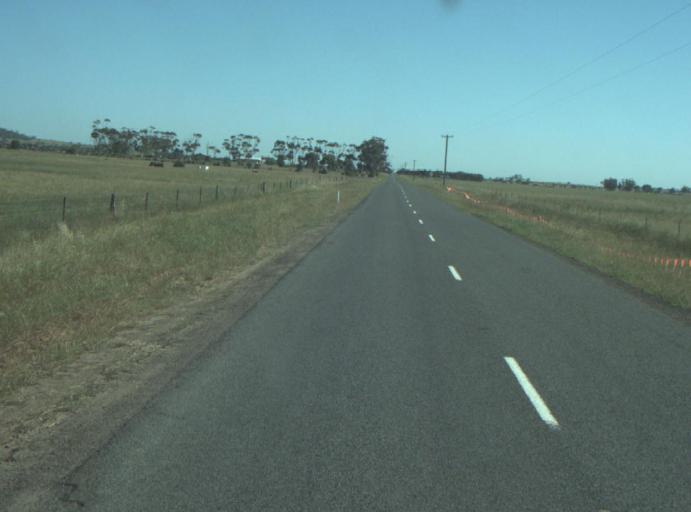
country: AU
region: Victoria
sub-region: Wyndham
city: Little River
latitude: -37.9721
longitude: 144.4612
